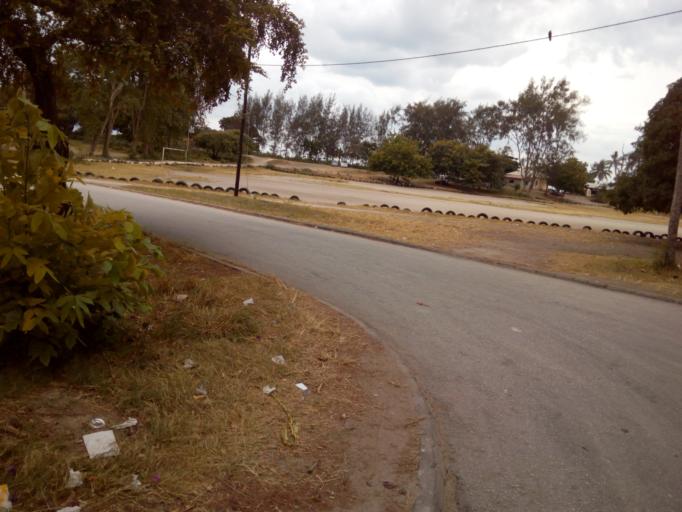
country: TZ
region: Zanzibar Urban/West
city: Zanzibar
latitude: -6.1730
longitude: 39.1960
